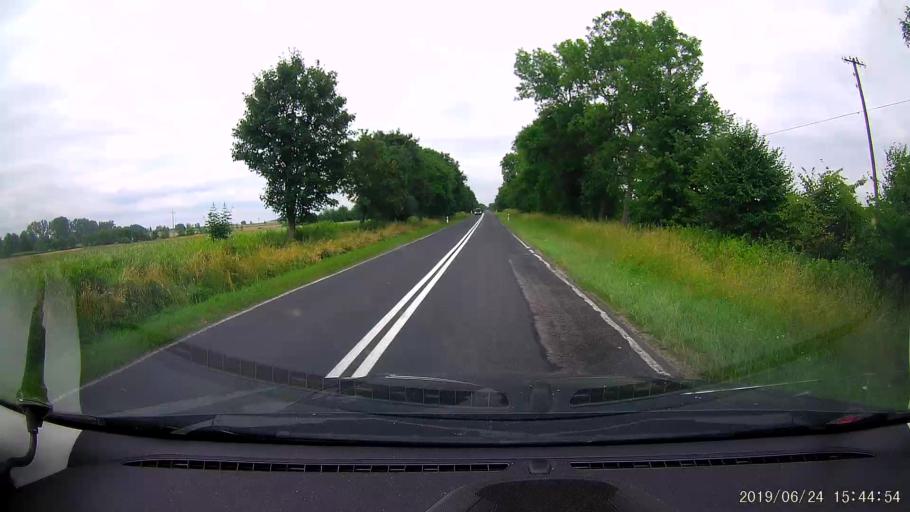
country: PL
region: Subcarpathian Voivodeship
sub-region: Powiat lubaczowski
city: Oleszyce
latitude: 50.1417
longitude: 22.9714
